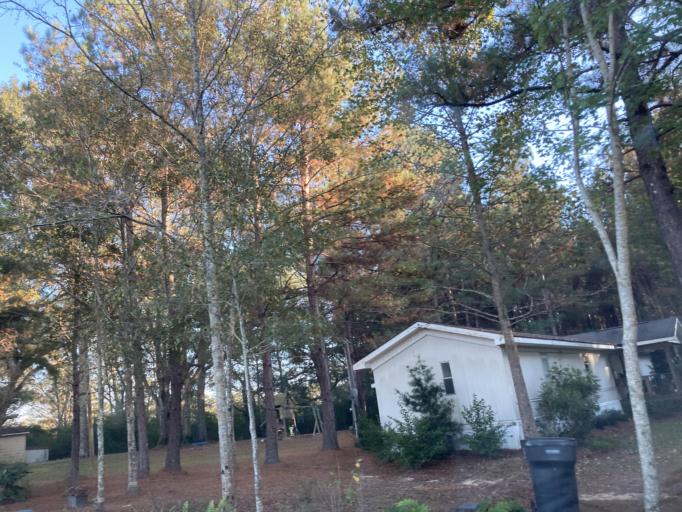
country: US
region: Mississippi
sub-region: Lamar County
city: Sumrall
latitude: 31.3973
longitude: -89.6207
